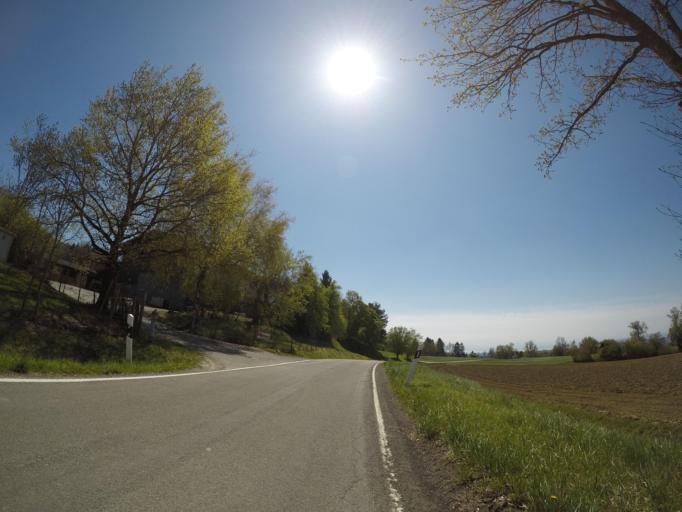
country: DE
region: Baden-Wuerttemberg
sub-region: Tuebingen Region
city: Markdorf
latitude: 47.7399
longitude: 9.3839
